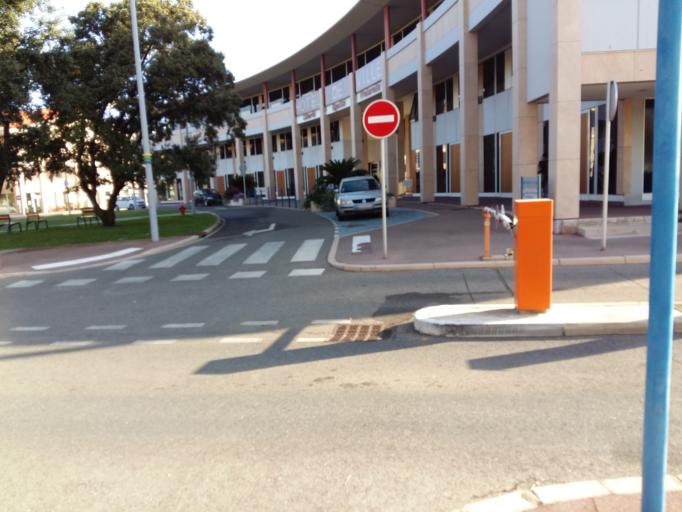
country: FR
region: Provence-Alpes-Cote d'Azur
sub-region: Departement des Bouches-du-Rhone
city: Martigues
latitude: 43.4055
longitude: 5.0478
